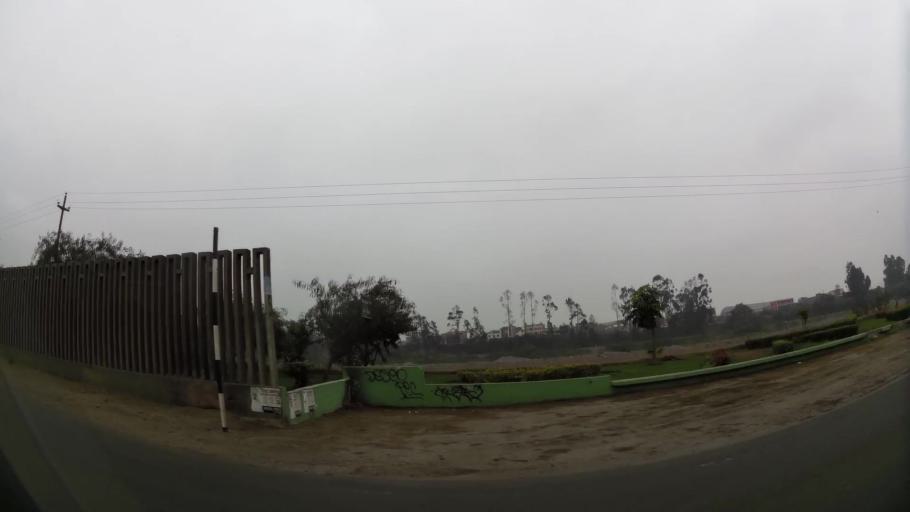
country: PE
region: Lima
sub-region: Lima
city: Vitarte
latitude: -12.0211
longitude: -76.9331
